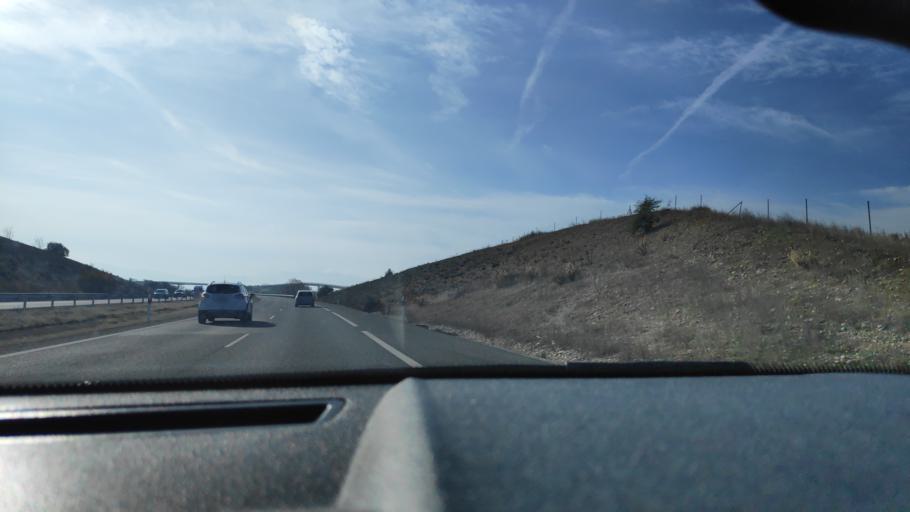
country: ES
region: Andalusia
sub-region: Provincia de Jaen
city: Jaen
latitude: 37.8554
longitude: -3.7654
